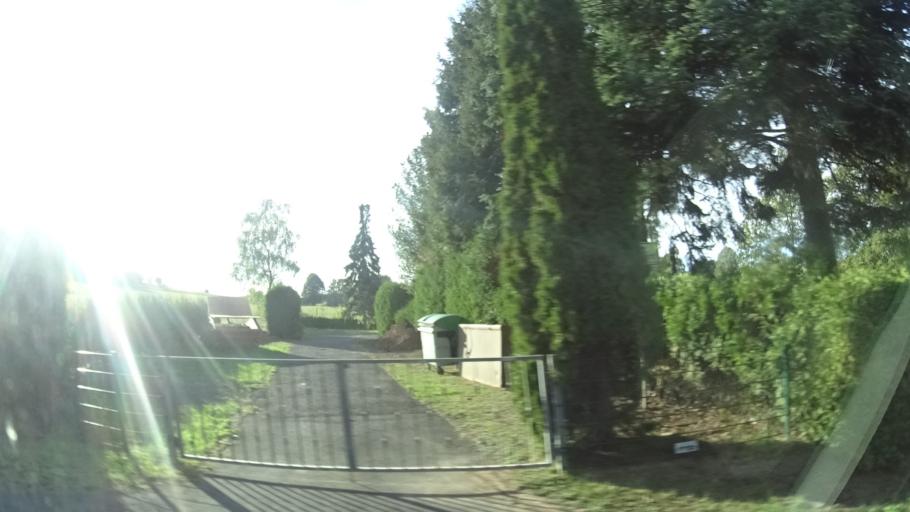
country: DE
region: Hesse
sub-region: Regierungsbezirk Giessen
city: Freiensteinau
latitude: 50.4105
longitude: 9.4608
